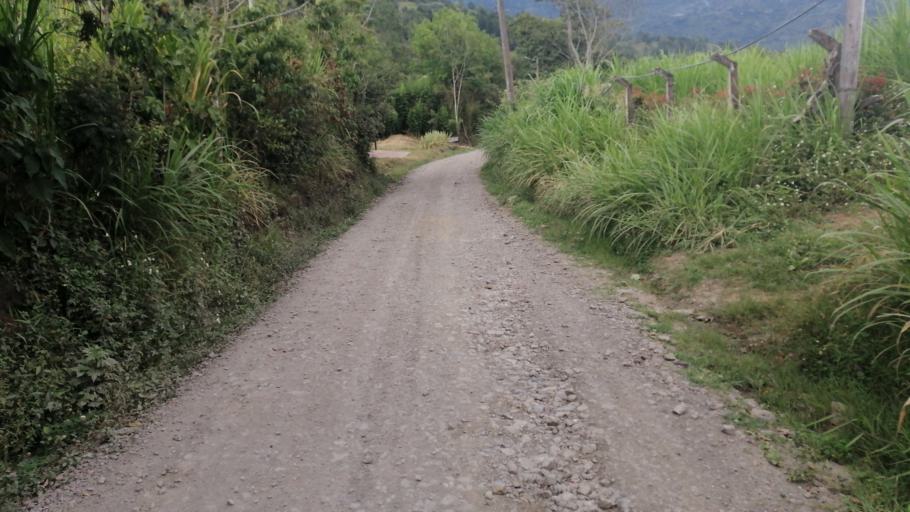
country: CO
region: Cundinamarca
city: Tenza
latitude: 5.0554
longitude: -73.4264
